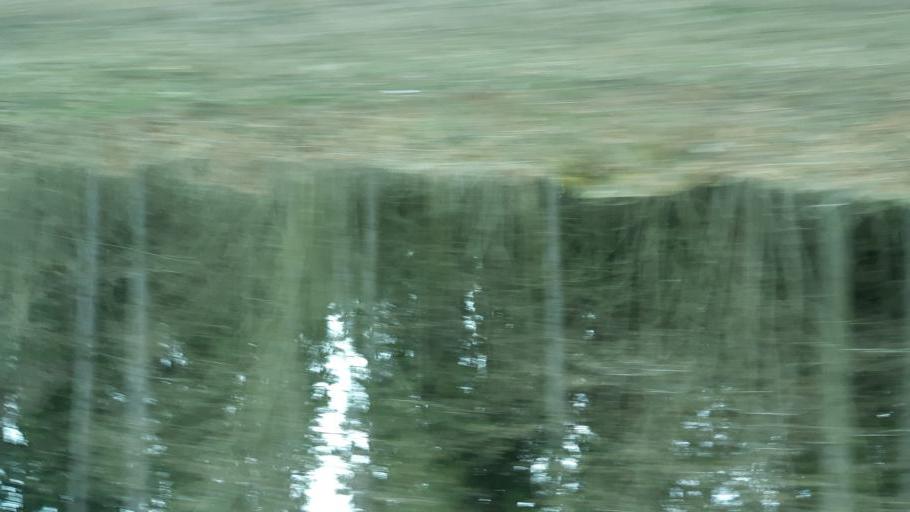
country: PL
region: Podlasie
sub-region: Suwalki
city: Suwalki
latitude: 54.2813
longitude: 22.9473
